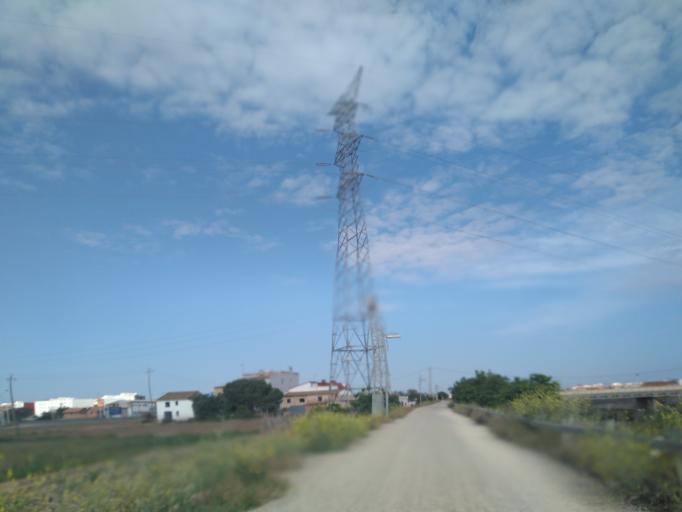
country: ES
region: Valencia
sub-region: Provincia de Valencia
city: Alboraya
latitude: 39.5044
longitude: -0.3430
